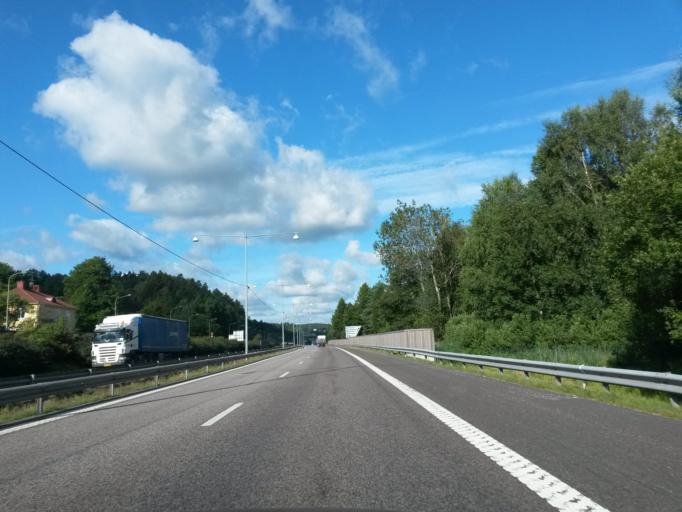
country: SE
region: Vaestra Goetaland
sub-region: Partille Kommun
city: Furulund
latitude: 57.7428
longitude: 12.1484
